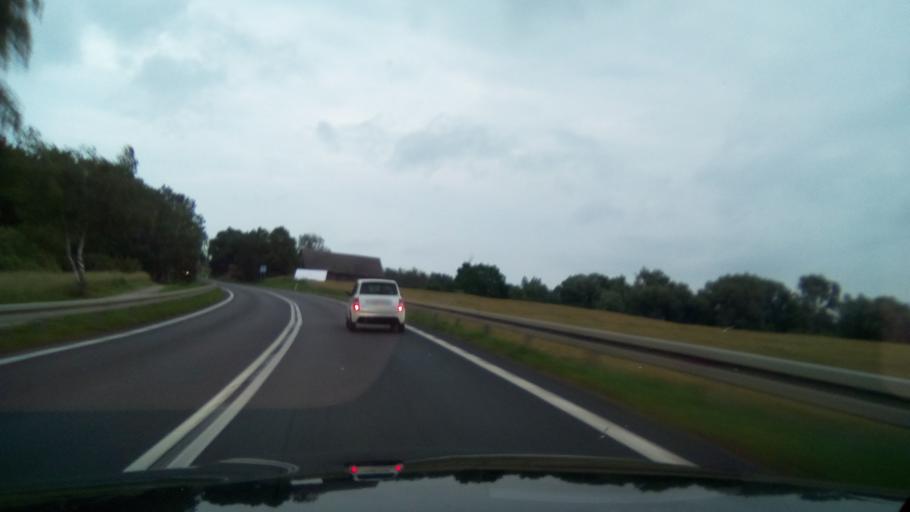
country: PL
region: Greater Poland Voivodeship
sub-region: Powiat gnieznienski
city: Lubowo
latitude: 52.5072
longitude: 17.3751
